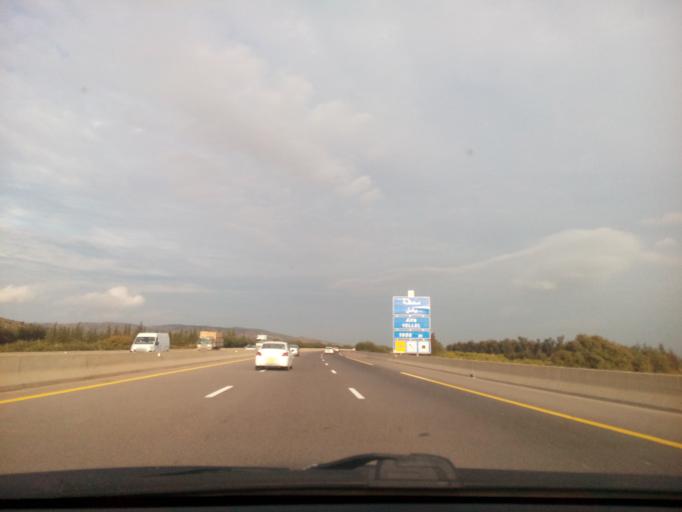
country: DZ
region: Relizane
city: Relizane
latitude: 35.7868
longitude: 0.3905
